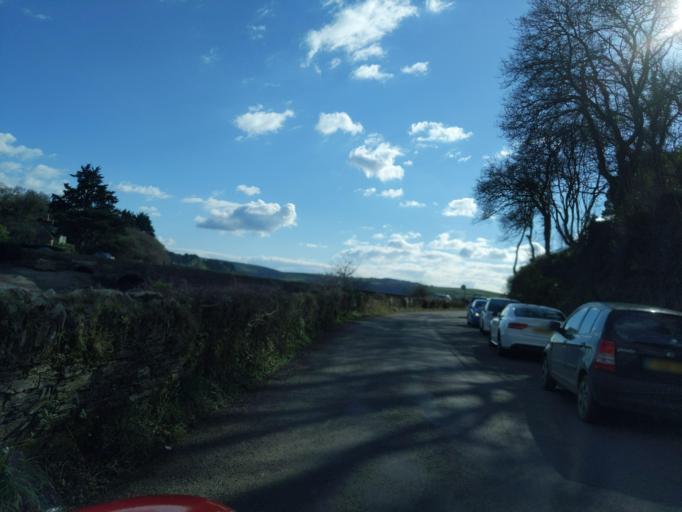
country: GB
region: England
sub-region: Devon
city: Kingsbridge
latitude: 50.2759
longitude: -3.7623
